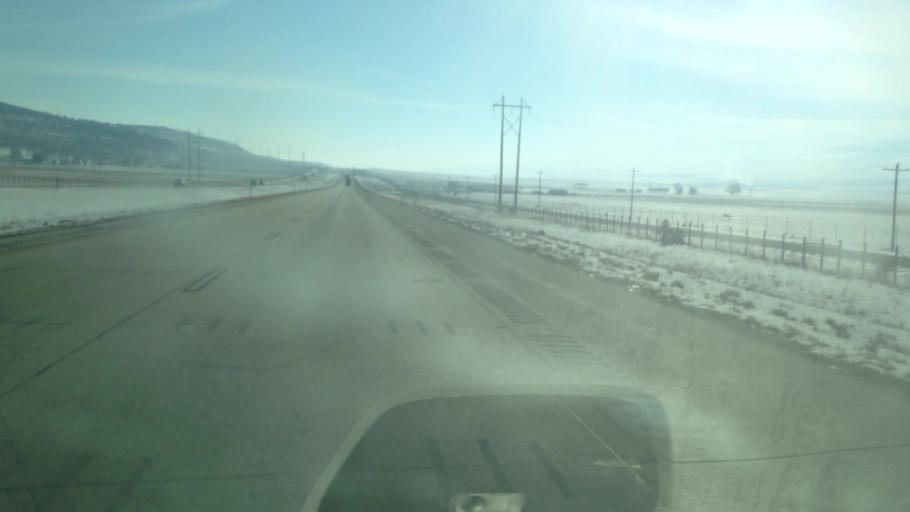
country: US
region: Utah
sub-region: Box Elder County
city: Garland
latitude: 41.9282
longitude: -112.1722
